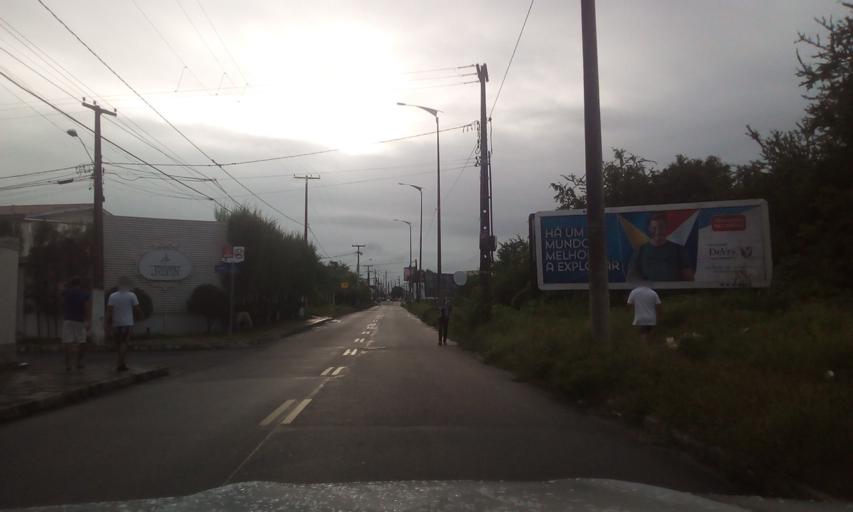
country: BR
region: Paraiba
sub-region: Joao Pessoa
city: Joao Pessoa
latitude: -7.0936
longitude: -34.8445
